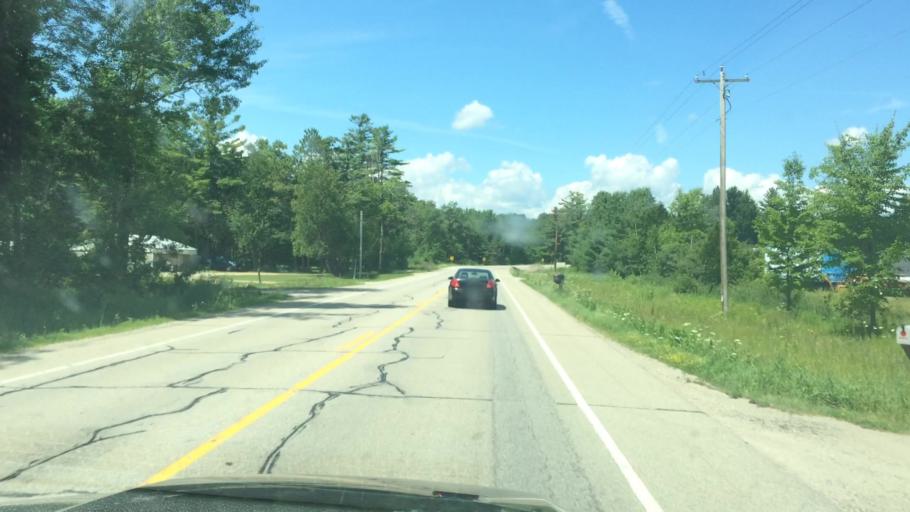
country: US
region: Wisconsin
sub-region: Marinette County
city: Peshtigo
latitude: 45.1005
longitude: -87.7399
